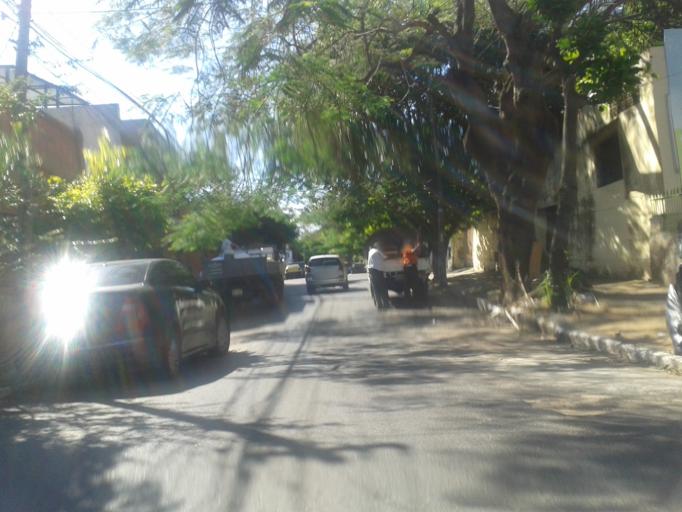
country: PY
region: Asuncion
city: Asuncion
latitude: -25.2944
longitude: -57.6387
